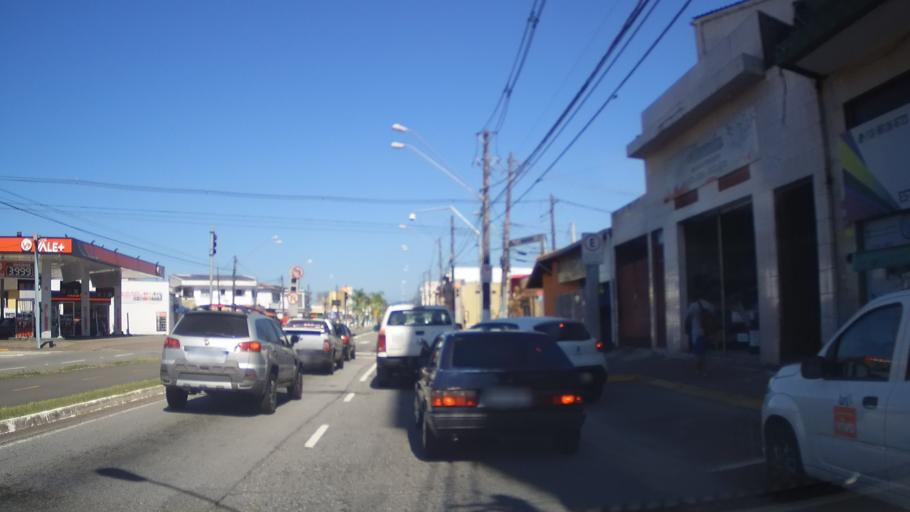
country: BR
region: Sao Paulo
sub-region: Praia Grande
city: Praia Grande
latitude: -24.0291
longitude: -46.4882
